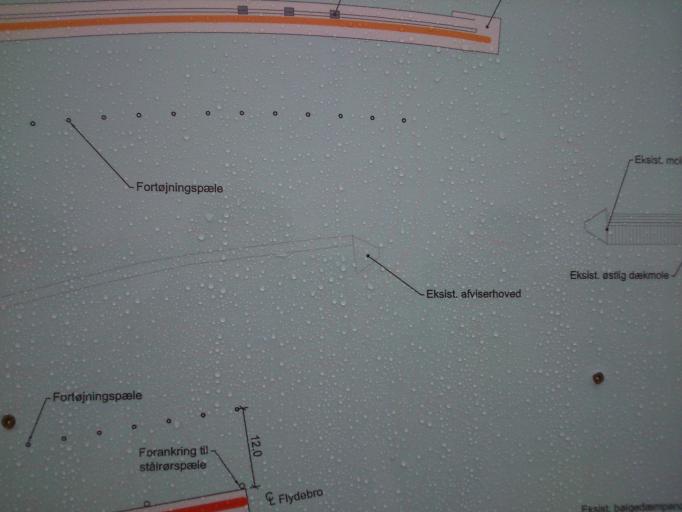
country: DK
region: Central Jutland
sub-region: Lemvig Kommune
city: Lemvig
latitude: 56.5501
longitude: 8.3057
